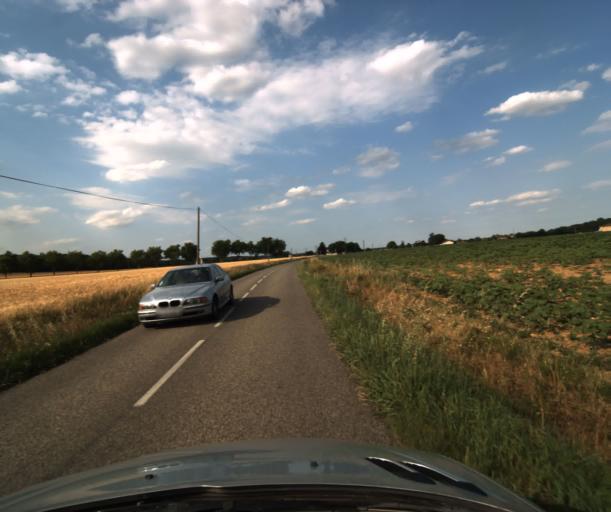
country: FR
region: Midi-Pyrenees
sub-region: Departement de la Haute-Garonne
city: Fonsorbes
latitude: 43.5177
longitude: 1.2288
